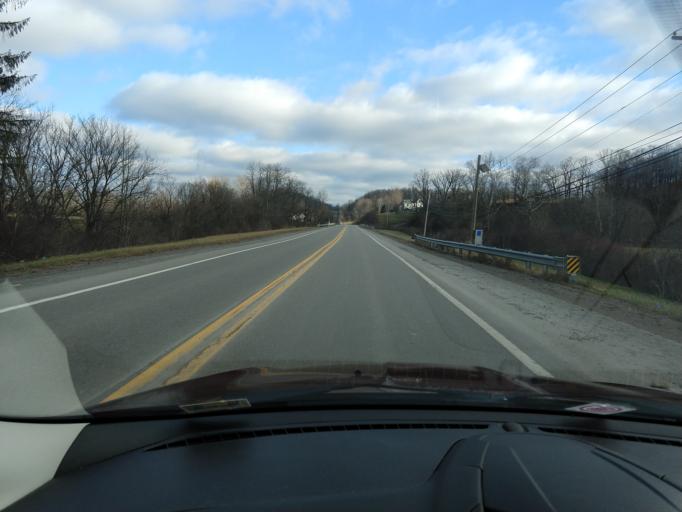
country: US
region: West Virginia
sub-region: Randolph County
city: Elkins
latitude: 38.8078
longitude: -79.8837
